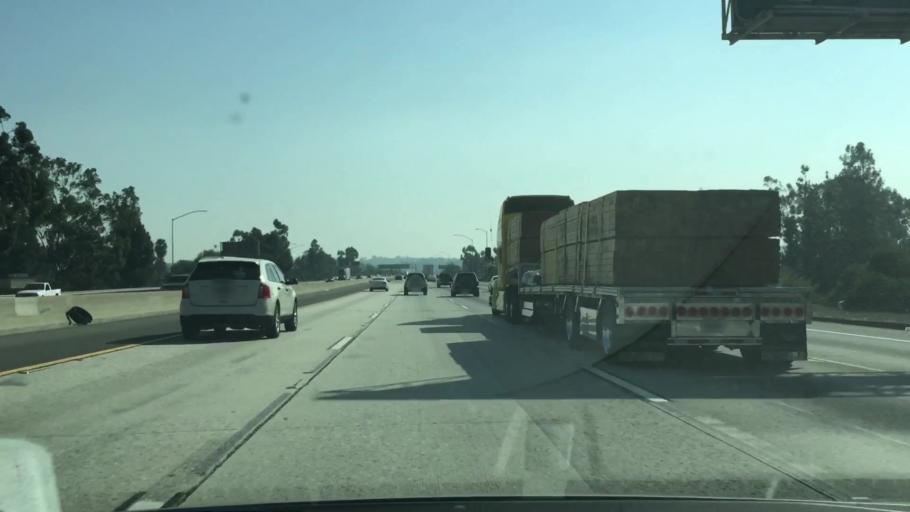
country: US
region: California
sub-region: Los Angeles County
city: San Dimas
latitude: 34.1082
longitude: -117.8225
